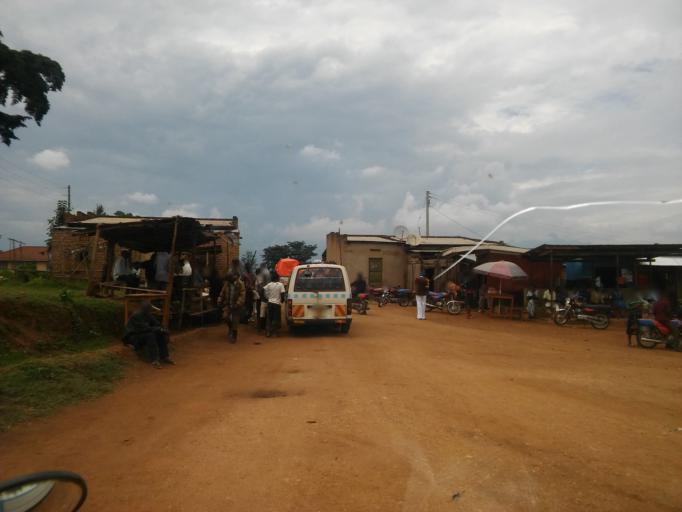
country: UG
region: Eastern Region
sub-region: Bududa District
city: Bududa
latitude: 0.9497
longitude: 34.2747
